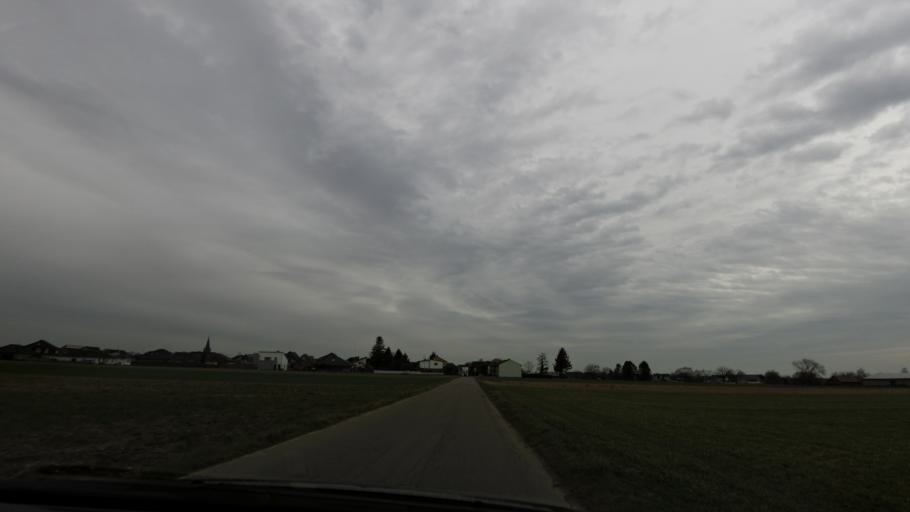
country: DE
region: North Rhine-Westphalia
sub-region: Regierungsbezirk Koln
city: Ubach-Palenberg
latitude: 50.9294
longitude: 6.0810
